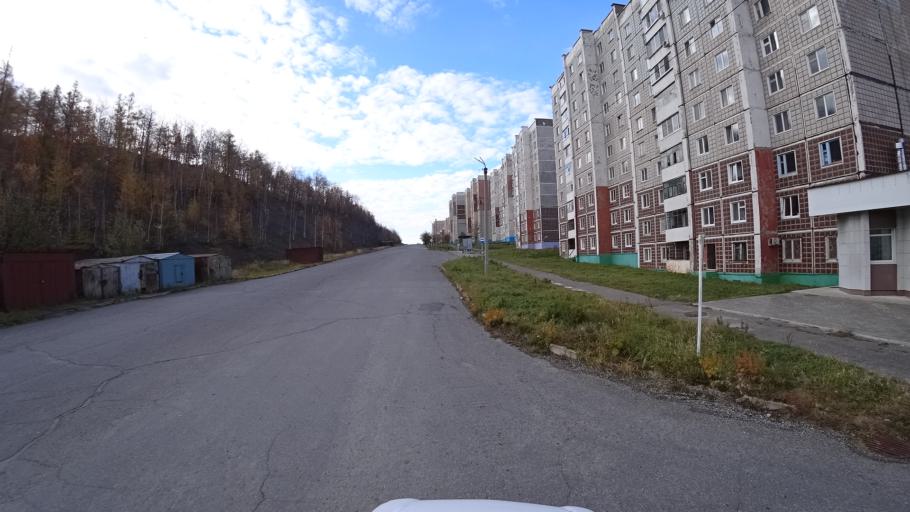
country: RU
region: Khabarovsk Krai
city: Amursk
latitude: 50.2484
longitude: 136.9228
